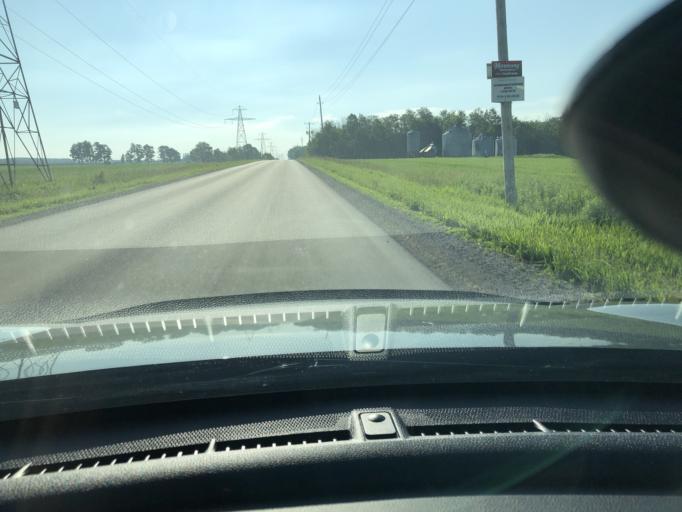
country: CA
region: Ontario
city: Stratford
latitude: 43.3881
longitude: -80.8555
